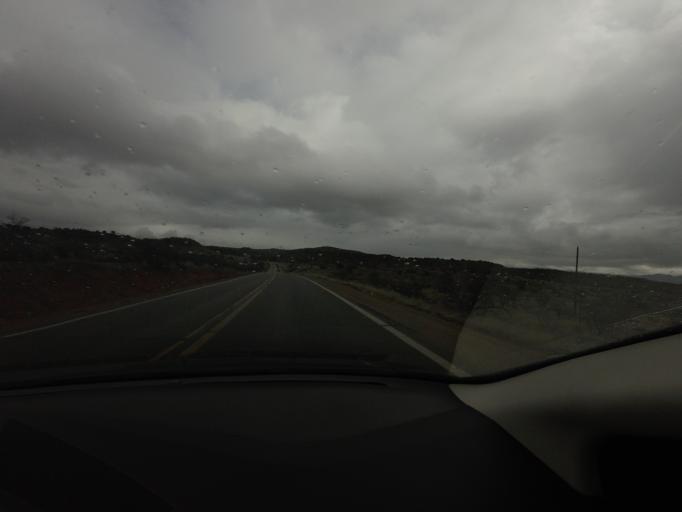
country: US
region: Arizona
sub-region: Yavapai County
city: Cornville
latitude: 34.7077
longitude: -111.8769
